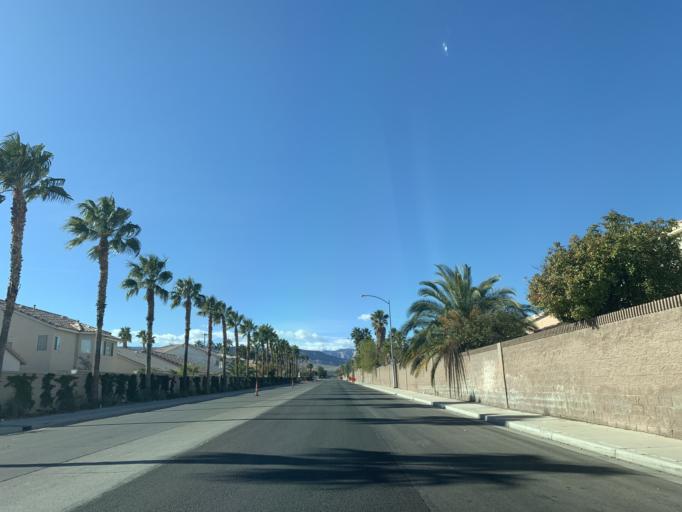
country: US
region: Nevada
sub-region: Clark County
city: Summerlin South
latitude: 36.1206
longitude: -115.3037
